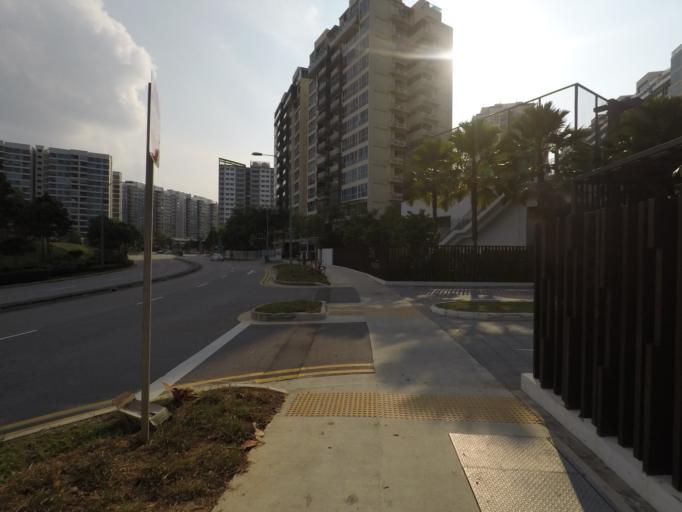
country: SG
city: Singapore
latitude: 1.3591
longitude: 103.9412
